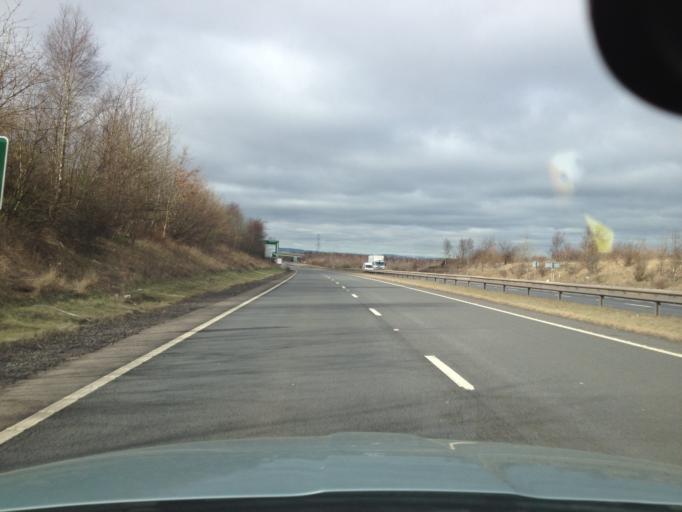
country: GB
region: Scotland
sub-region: East Lothian
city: Tranent
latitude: 55.9526
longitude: -2.9438
